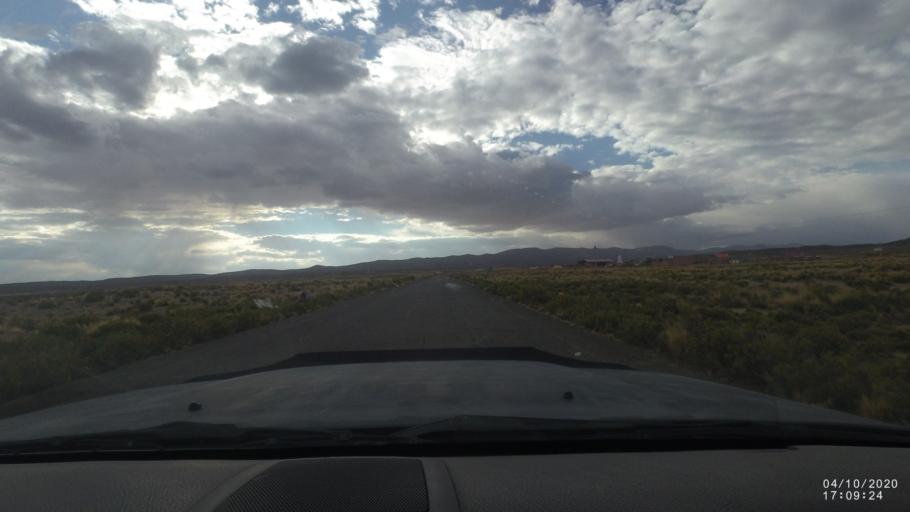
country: BO
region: Oruro
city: Oruro
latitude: -18.3392
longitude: -67.5830
